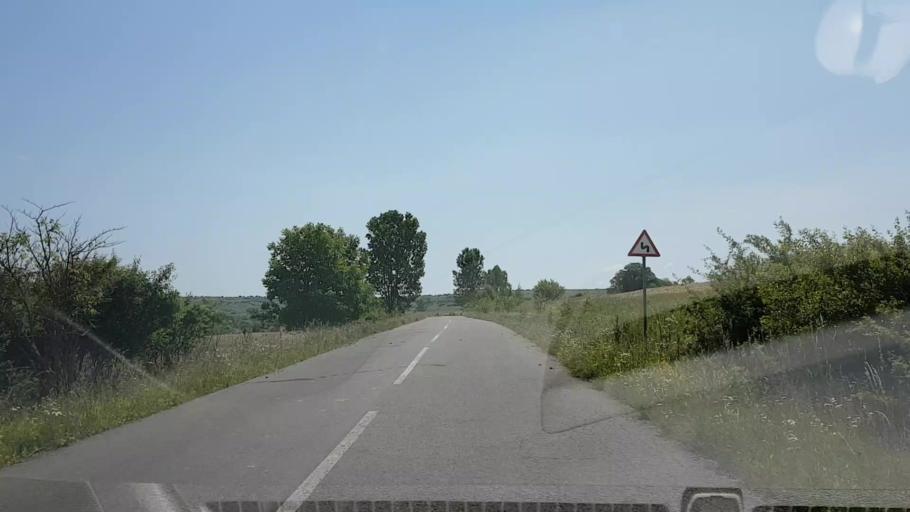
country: RO
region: Sibiu
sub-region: Comuna Merghindeal
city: Merghindeal
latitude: 45.9557
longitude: 24.7734
